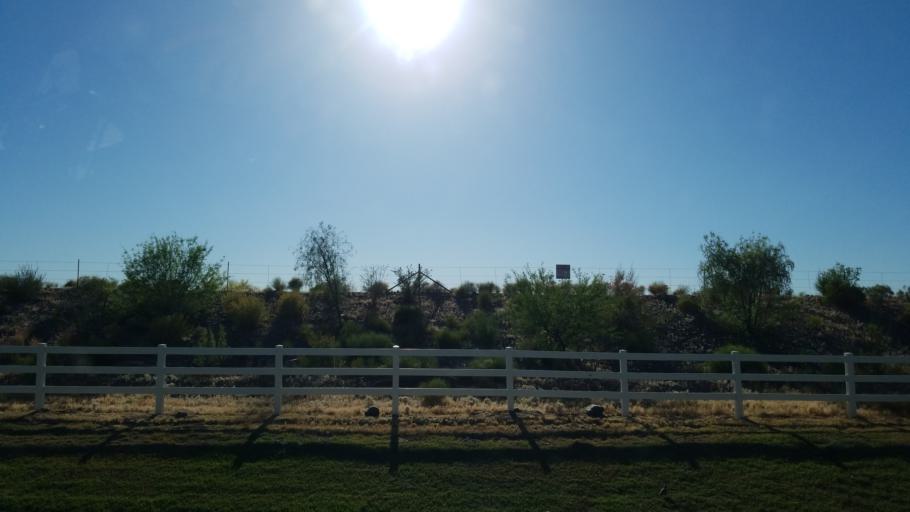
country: US
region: Arizona
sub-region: Maricopa County
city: Youngtown
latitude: 33.5742
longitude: -112.3114
